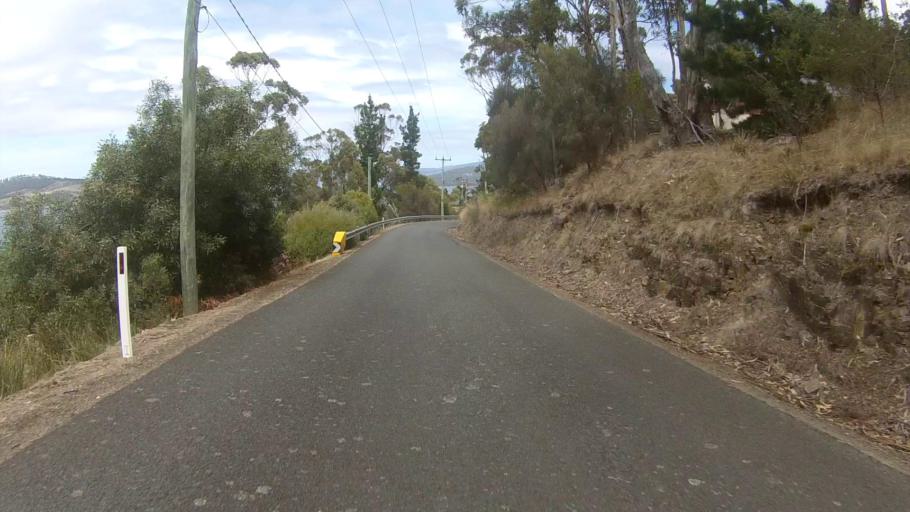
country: AU
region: Tasmania
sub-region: Kingborough
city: Blackmans Bay
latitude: -43.0533
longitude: 147.3382
